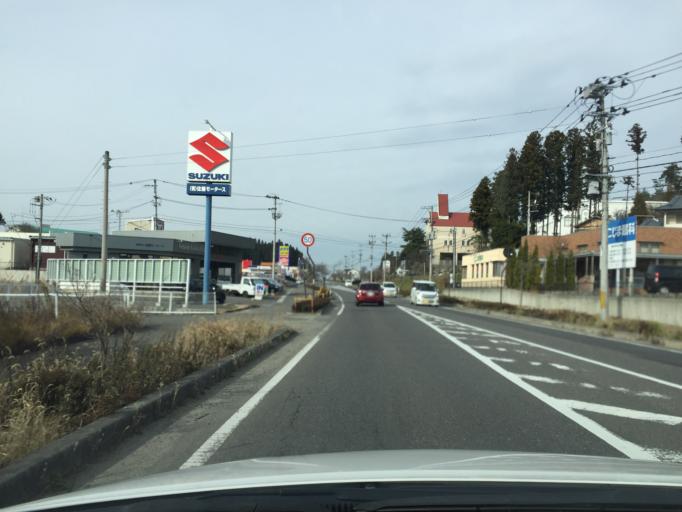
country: JP
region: Fukushima
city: Funehikimachi-funehiki
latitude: 37.4469
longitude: 140.5839
